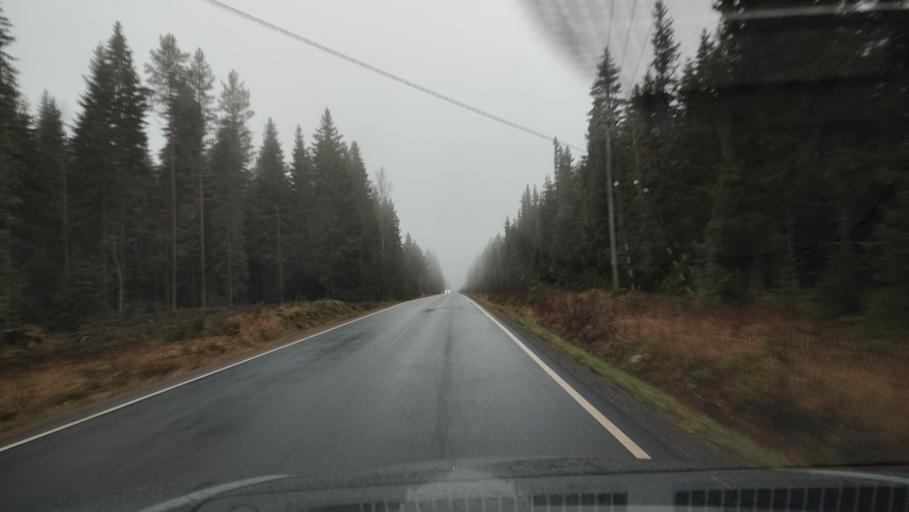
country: FI
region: Southern Ostrobothnia
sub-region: Suupohja
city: Karijoki
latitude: 62.1808
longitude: 21.7754
